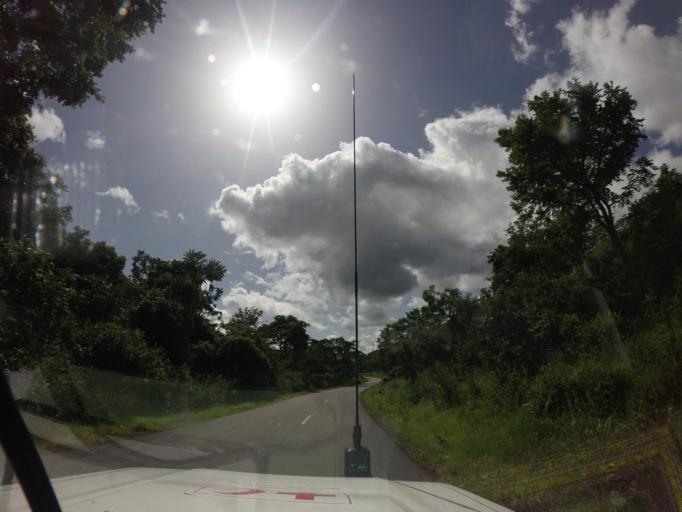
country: GN
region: Mamou
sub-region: Mamou Prefecture
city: Mamou
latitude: 10.3358
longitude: -12.0328
